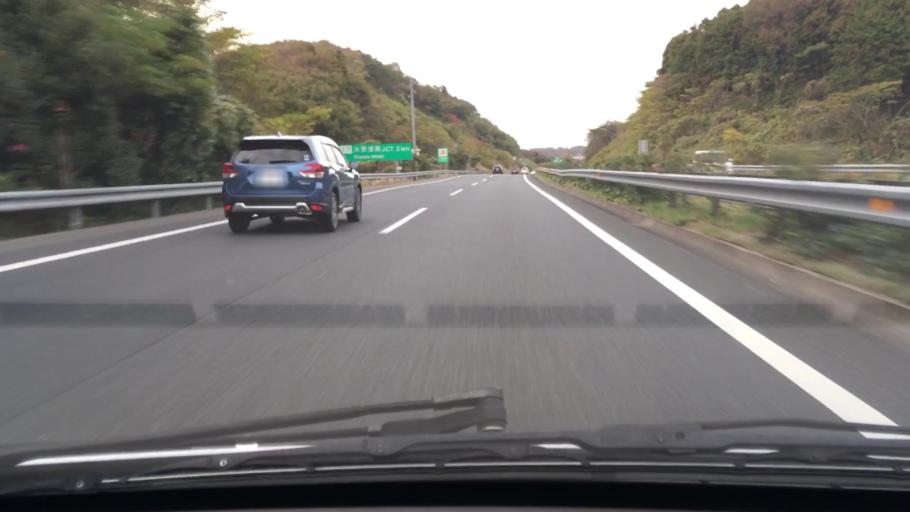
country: JP
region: Chiba
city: Kisarazu
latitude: 35.3335
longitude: 139.9453
